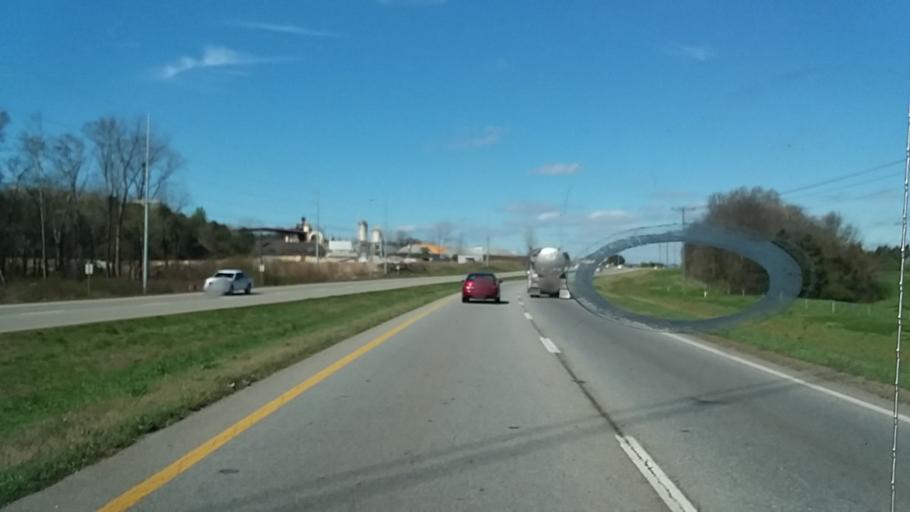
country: US
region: Alabama
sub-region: Morgan County
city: Trinity
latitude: 34.6204
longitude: -87.0747
